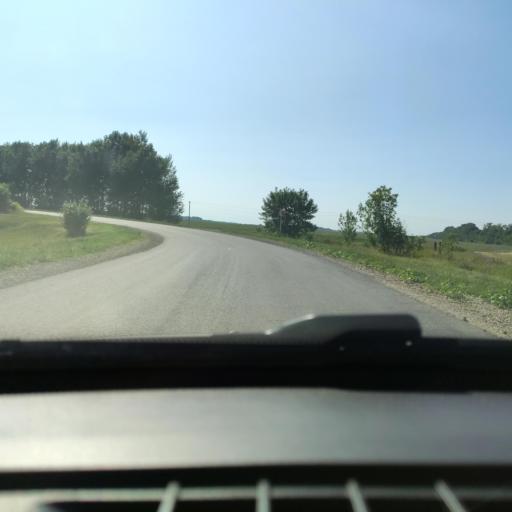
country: RU
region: Voronezj
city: Anna
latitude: 51.6482
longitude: 40.3701
